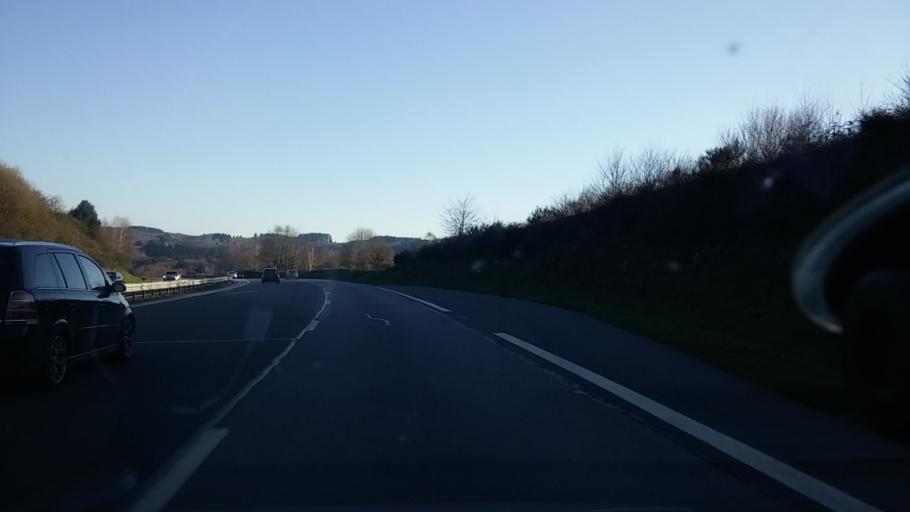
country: FR
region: Limousin
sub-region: Departement de la Haute-Vienne
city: Bessines-sur-Gartempe
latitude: 46.0829
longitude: 1.3565
